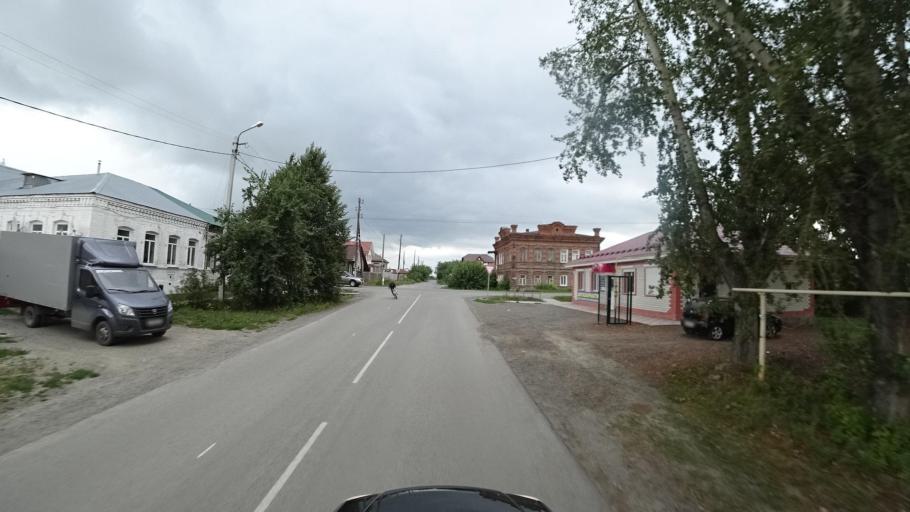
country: RU
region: Sverdlovsk
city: Kamyshlov
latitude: 56.8478
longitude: 62.6957
